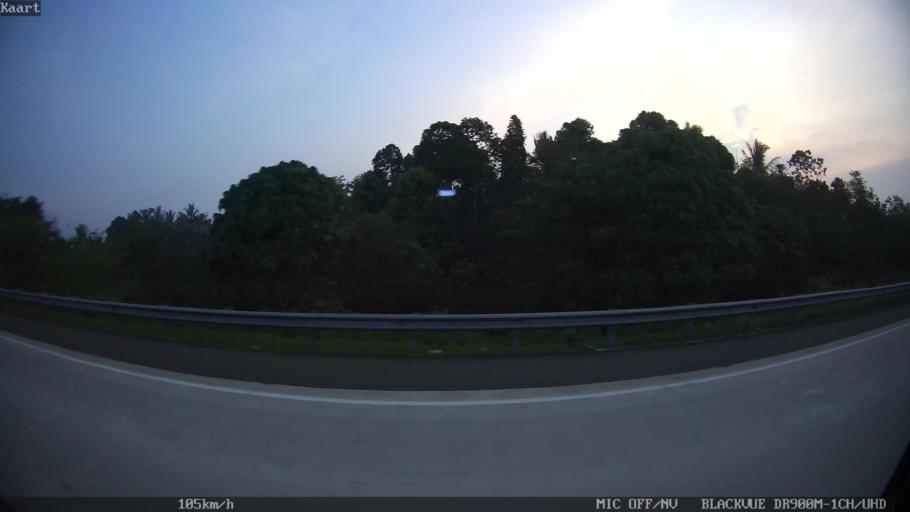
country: ID
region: Lampung
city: Kalianda
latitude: -5.6834
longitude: 105.6127
